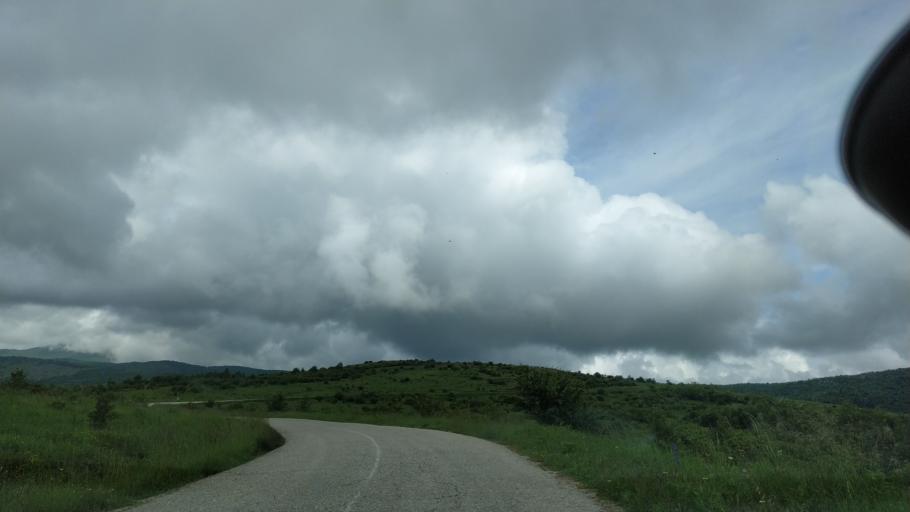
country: RS
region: Central Serbia
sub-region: Zajecarski Okrug
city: Soko Banja
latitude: 43.7045
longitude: 21.9377
